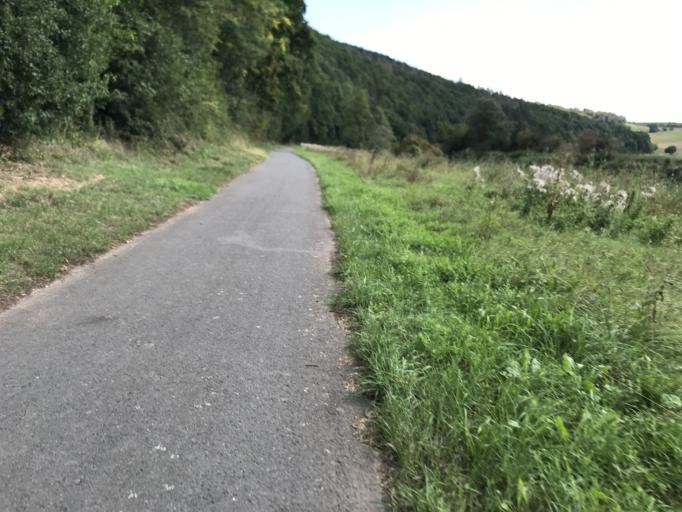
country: DE
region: Hesse
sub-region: Regierungsbezirk Kassel
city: Bad Sooden-Allendorf
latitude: 51.2382
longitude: 9.9969
